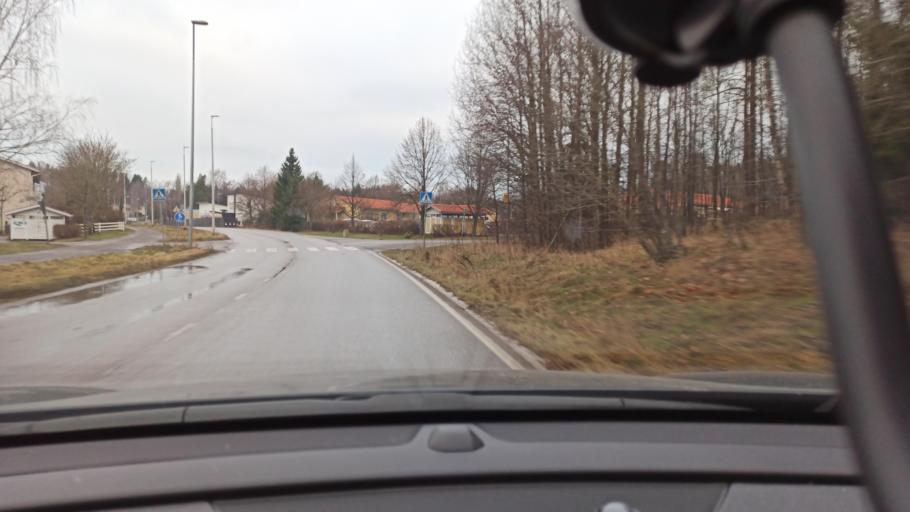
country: FI
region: Uusimaa
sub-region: Helsinki
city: Kirkkonummi
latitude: 60.1581
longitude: 24.5279
